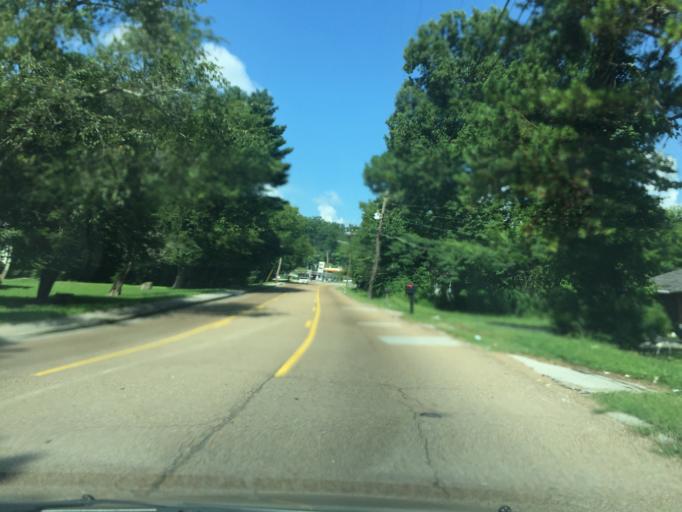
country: US
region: Tennessee
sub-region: Hamilton County
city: East Chattanooga
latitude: 35.0469
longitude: -85.2350
